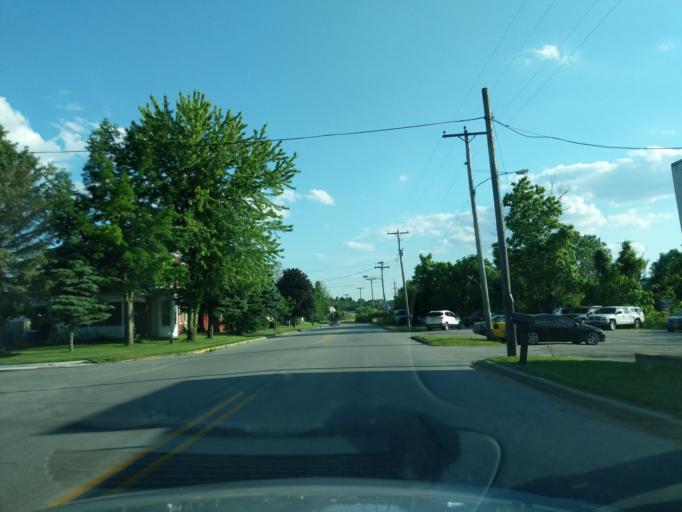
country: US
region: Indiana
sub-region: Whitley County
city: Columbia City
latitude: 41.1494
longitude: -85.4876
